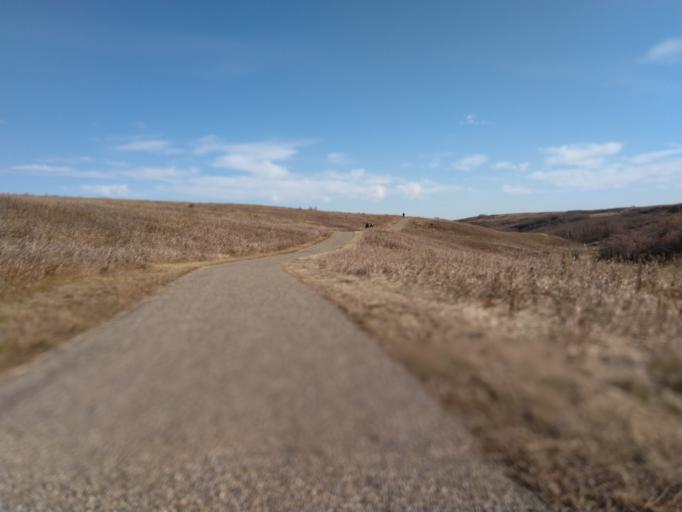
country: CA
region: Alberta
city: Calgary
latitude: 51.1207
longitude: -114.1160
